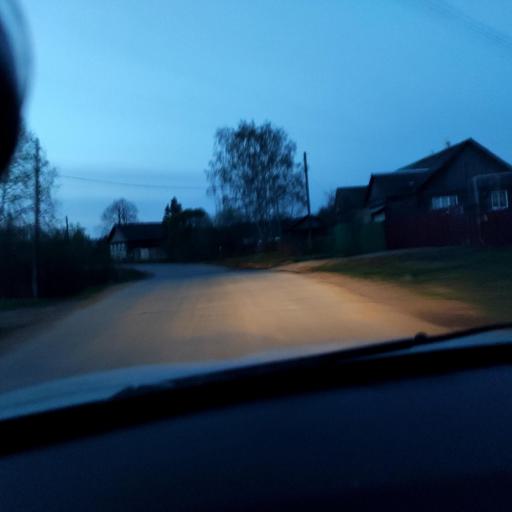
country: RU
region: Perm
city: Kukushtan
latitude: 57.4686
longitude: 56.5294
